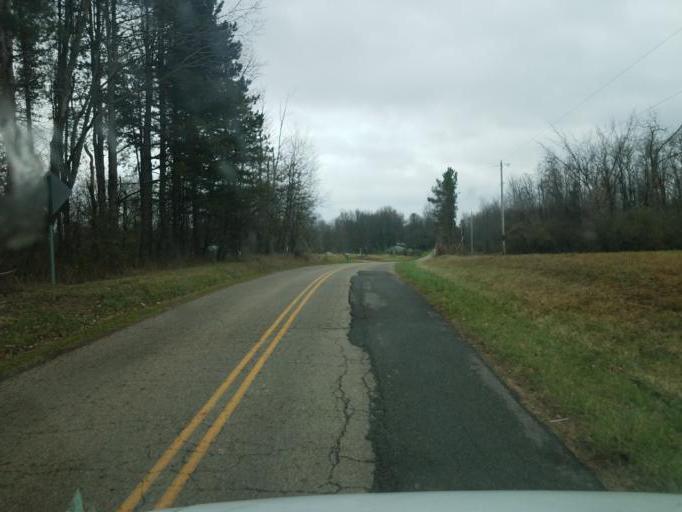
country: US
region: Ohio
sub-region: Knox County
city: Centerburg
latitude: 40.3734
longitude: -82.6179
